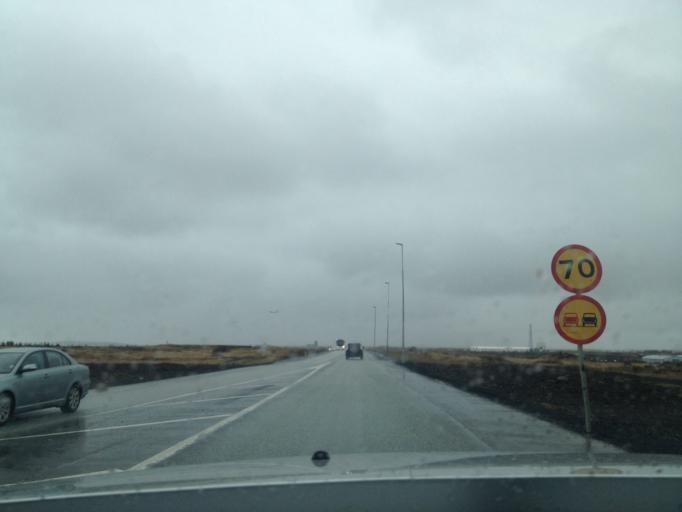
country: IS
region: Southern Peninsula
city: Reykjanesbaer
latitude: 63.9910
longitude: -22.5790
